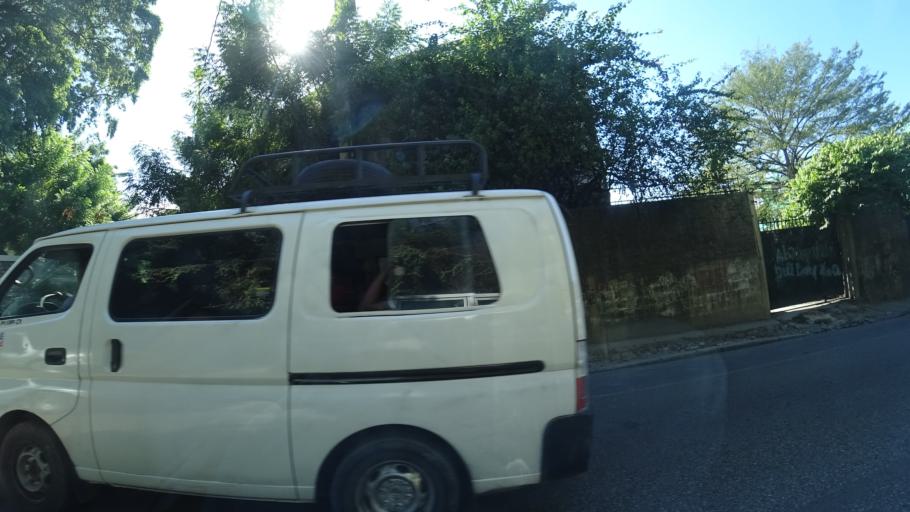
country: HT
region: Ouest
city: Delmas 73
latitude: 18.5360
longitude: -72.3113
